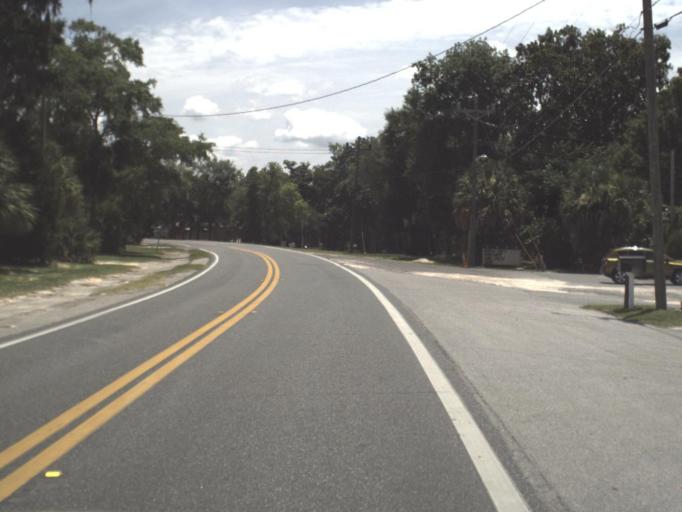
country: US
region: Florida
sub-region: Taylor County
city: Steinhatchee
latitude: 29.6676
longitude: -83.3725
